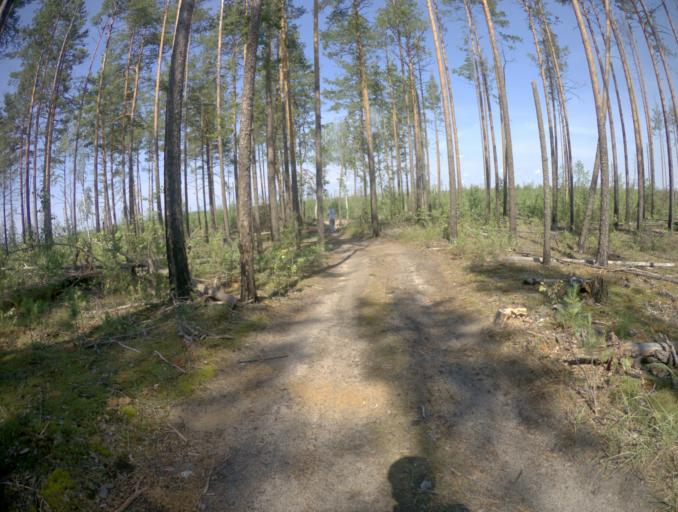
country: RU
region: Ivanovo
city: Talitsy
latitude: 56.4127
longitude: 42.2731
